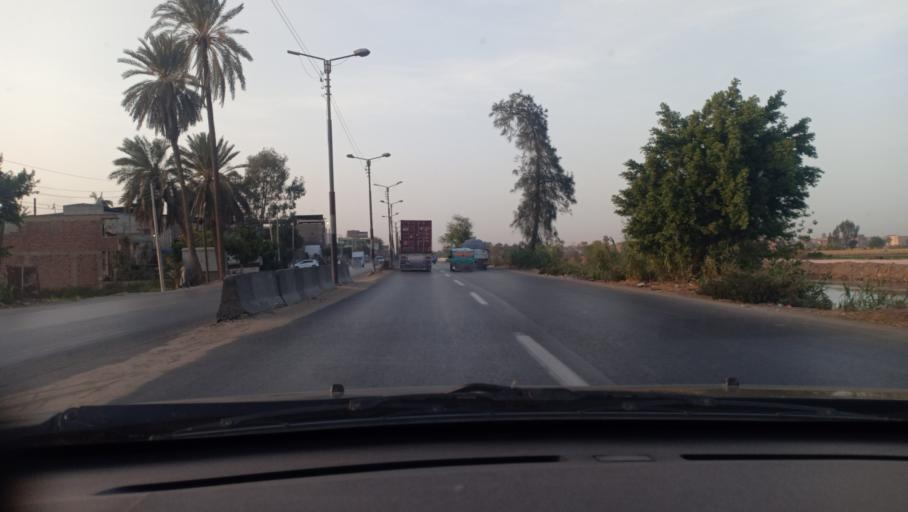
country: EG
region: Muhafazat al Gharbiyah
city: Zifta
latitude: 30.6587
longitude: 31.2844
